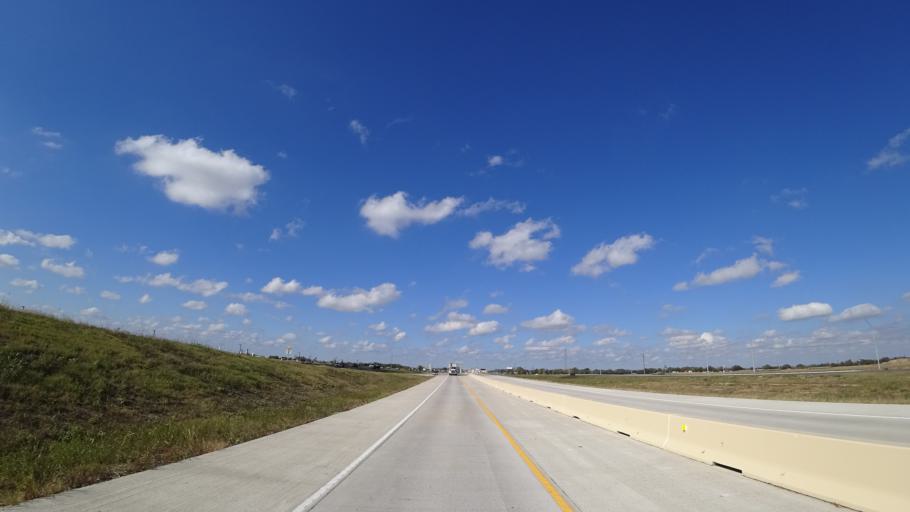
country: US
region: Texas
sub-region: Travis County
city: Hornsby Bend
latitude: 30.1983
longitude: -97.6304
